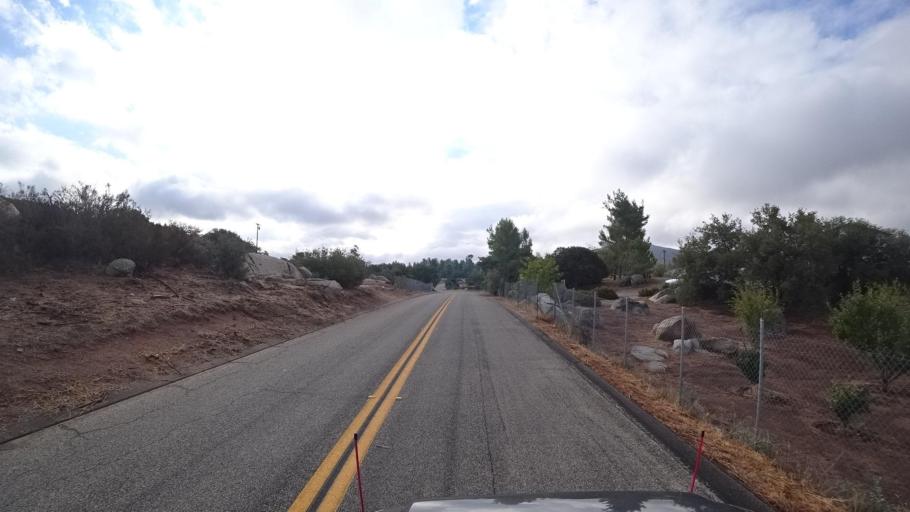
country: MX
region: Baja California
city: Tecate
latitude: 32.6391
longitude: -116.6371
